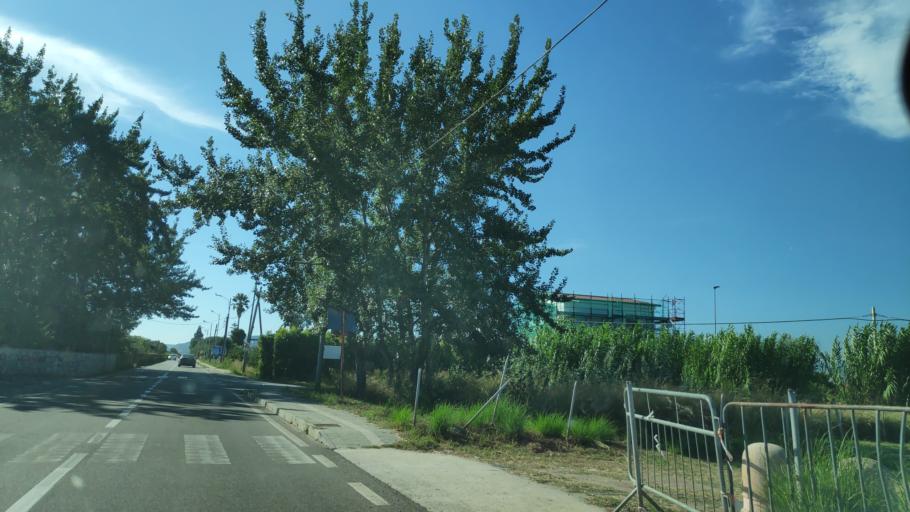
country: IT
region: Calabria
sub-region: Provincia di Catanzaro
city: Roccelletta
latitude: 38.8099
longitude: 16.5971
